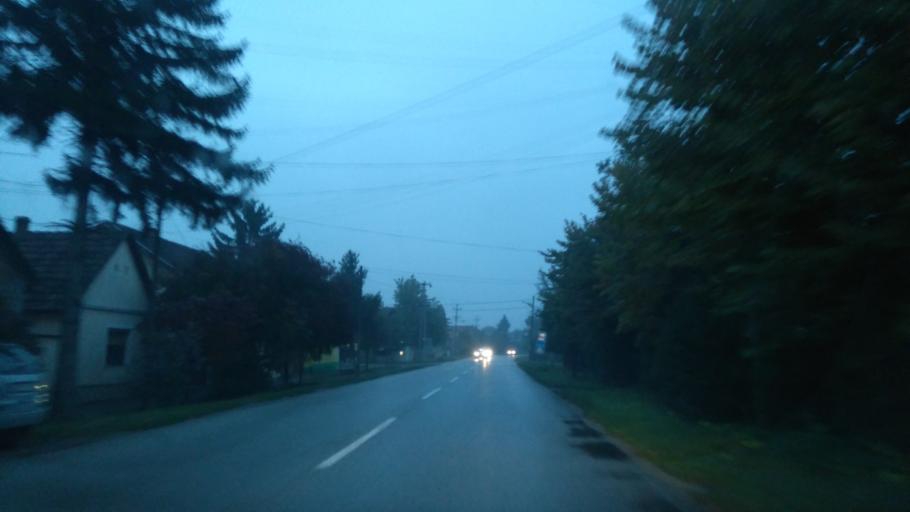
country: RS
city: Backo Petrovo Selo
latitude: 45.7095
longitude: 20.0876
